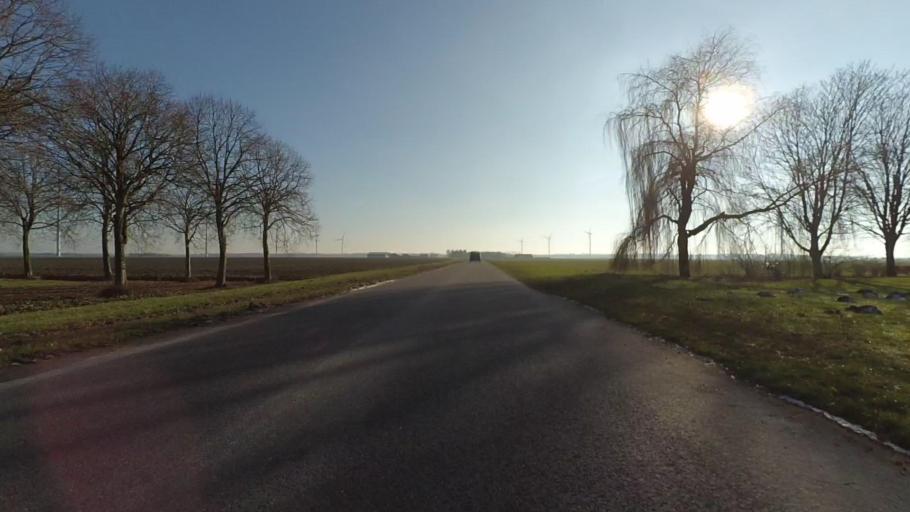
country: NL
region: Utrecht
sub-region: Gemeente Bunschoten
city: Spakenburg
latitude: 52.2930
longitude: 5.3926
